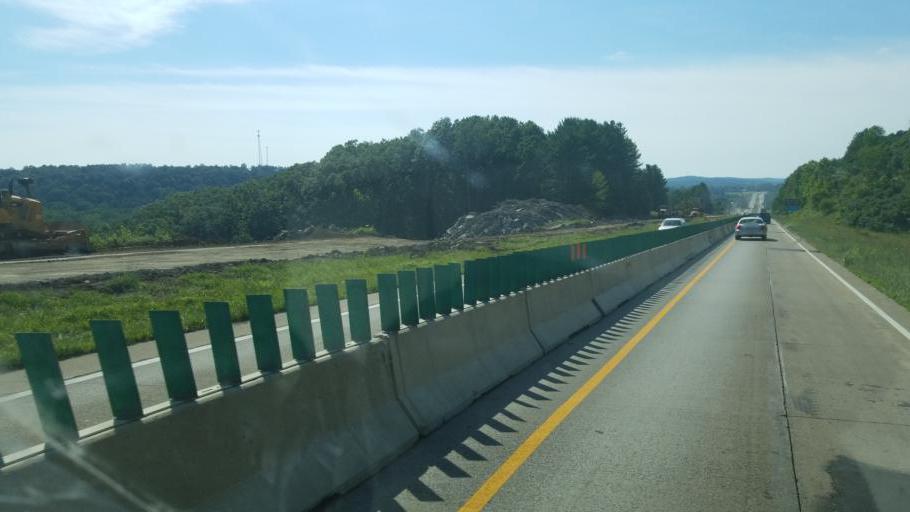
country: US
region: Ohio
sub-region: Athens County
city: Athens
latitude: 39.3552
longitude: -82.0952
